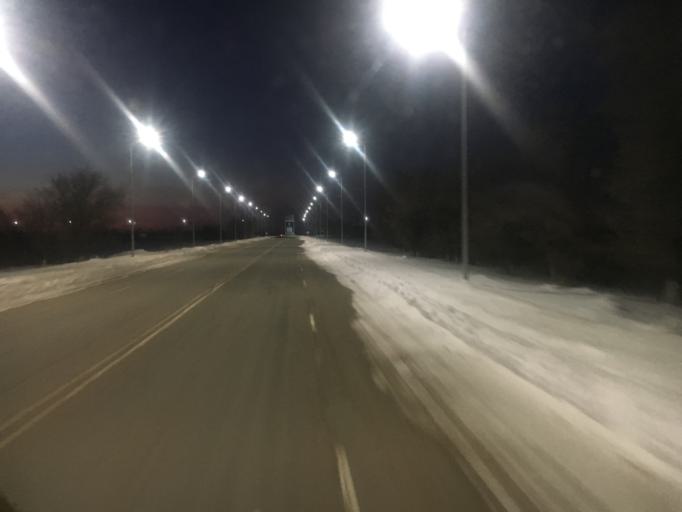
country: KZ
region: Batys Qazaqstan
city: Oral
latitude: 51.1629
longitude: 51.5270
